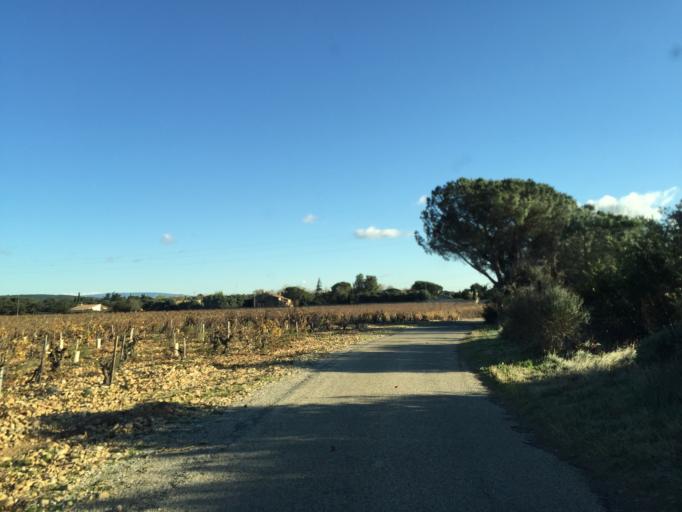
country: FR
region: Provence-Alpes-Cote d'Azur
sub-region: Departement du Vaucluse
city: Sorgues
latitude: 44.0283
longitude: 4.8508
